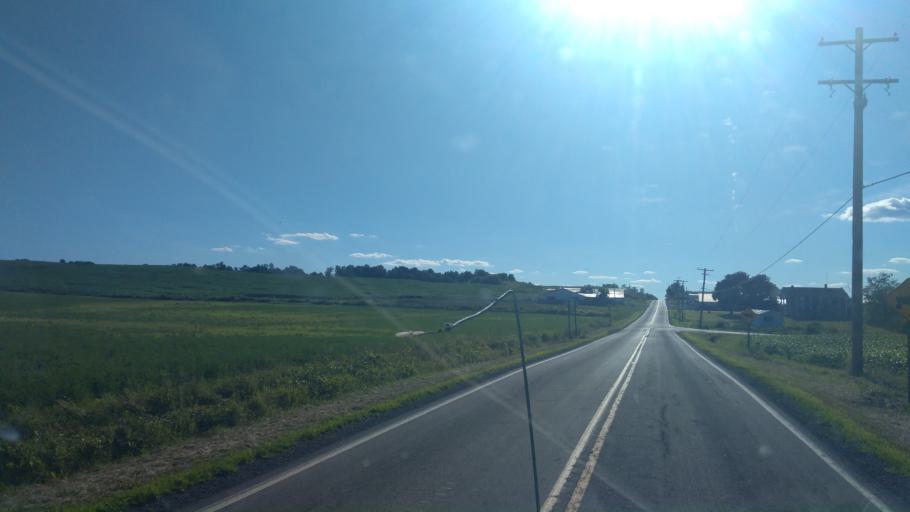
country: US
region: New York
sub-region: Wayne County
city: Lyons
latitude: 42.9950
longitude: -76.9262
